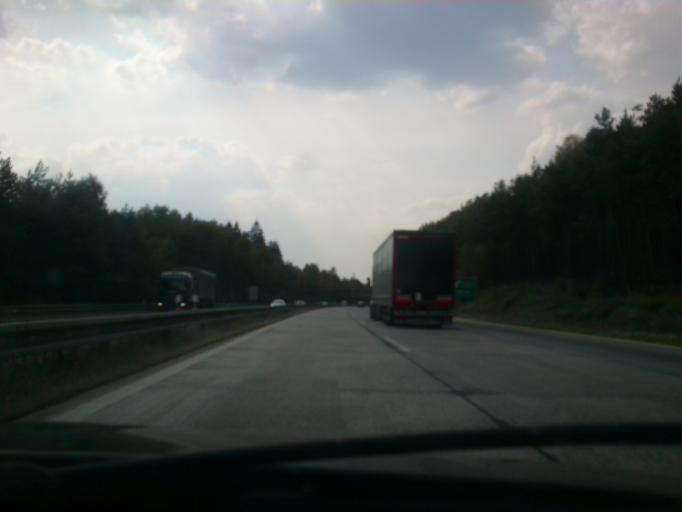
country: CZ
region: Central Bohemia
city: Trhovy Stepanov
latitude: 49.7495
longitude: 14.9899
